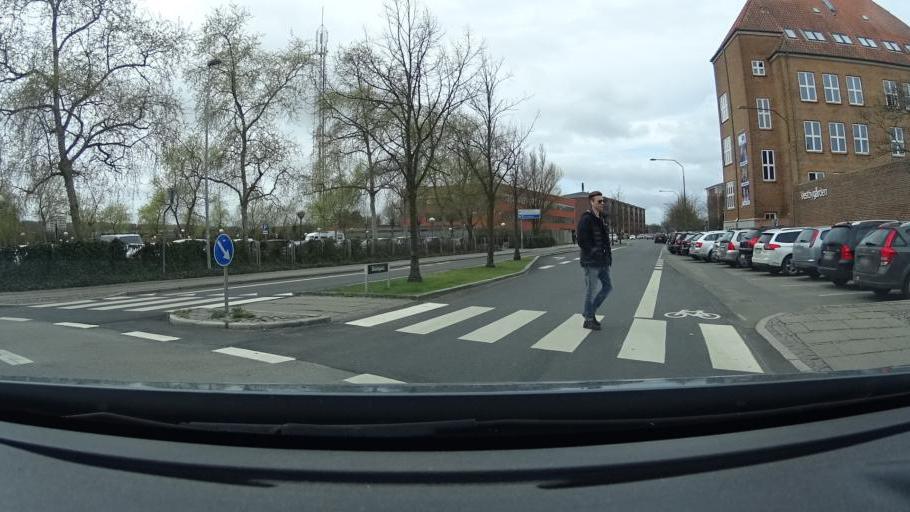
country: DK
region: South Denmark
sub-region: Vejle Kommune
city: Vejle
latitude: 55.7121
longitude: 9.5286
